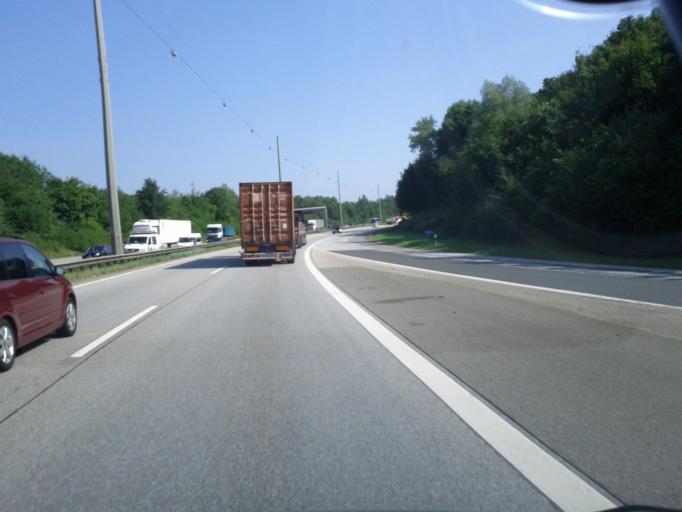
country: DE
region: Hamburg
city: Eidelstedt
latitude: 53.6188
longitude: 9.9130
